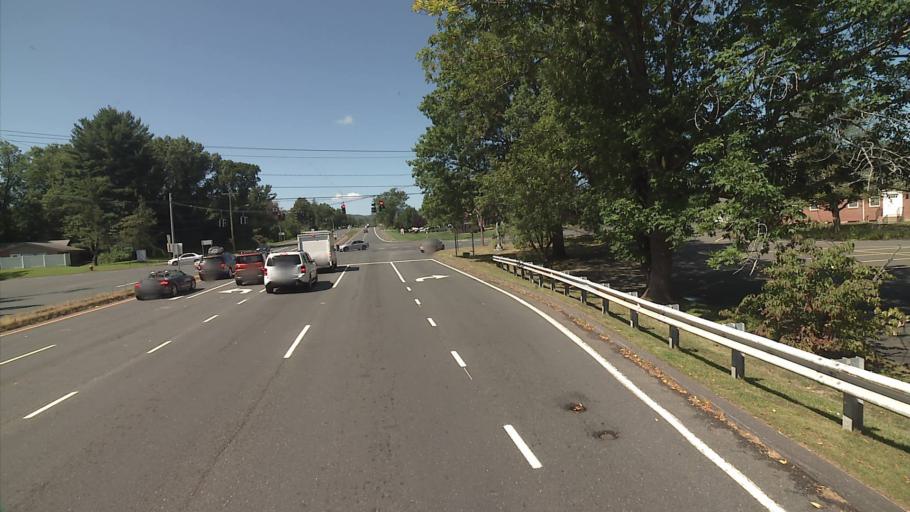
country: US
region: Connecticut
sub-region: Hartford County
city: Blue Hills
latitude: 41.8170
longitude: -72.7379
